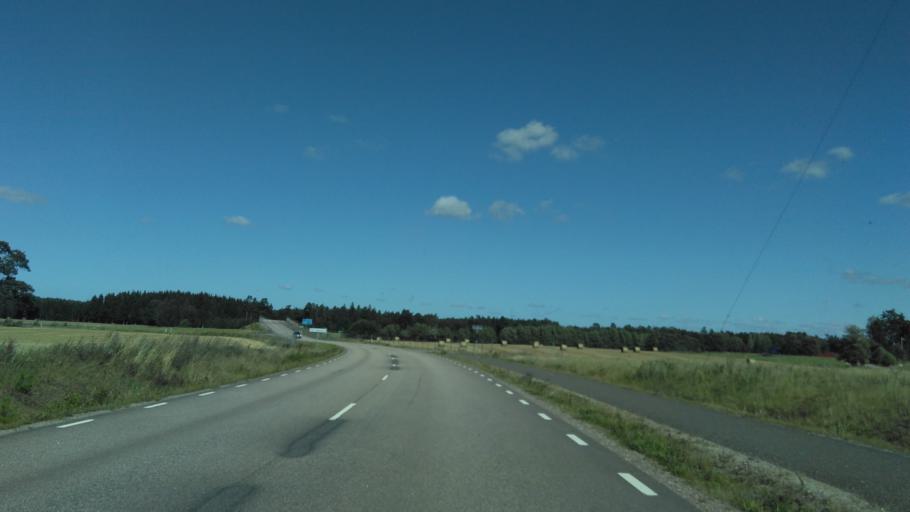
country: SE
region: Vaestra Goetaland
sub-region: Skara Kommun
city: Axvall
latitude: 58.3923
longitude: 13.5306
